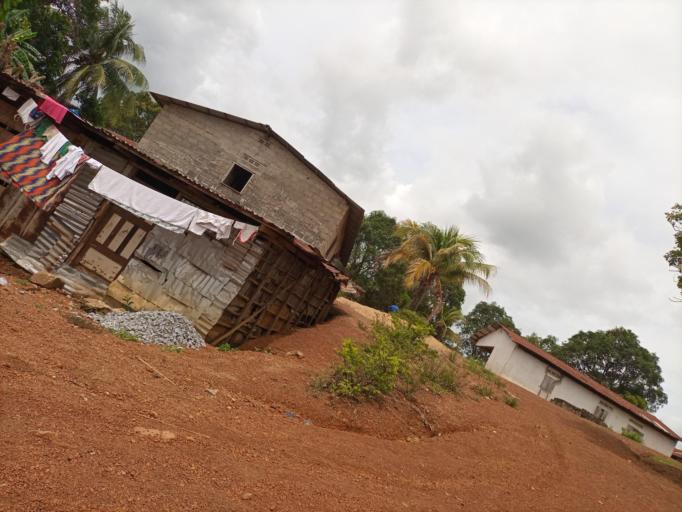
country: SL
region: Southern Province
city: Bo
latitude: 7.9703
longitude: -11.7166
